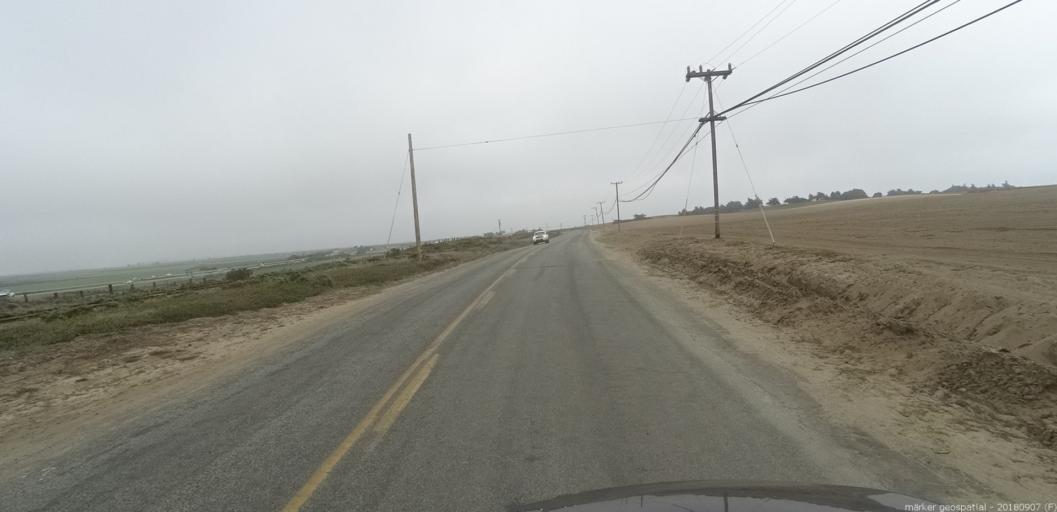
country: US
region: California
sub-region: Monterey County
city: Marina
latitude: 36.7168
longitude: -121.7917
